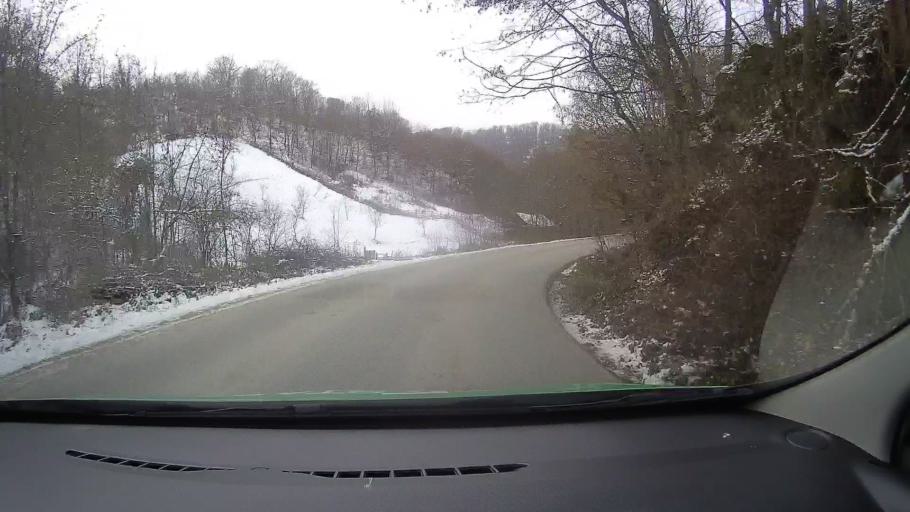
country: RO
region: Alba
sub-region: Oras Zlatna
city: Zlatna
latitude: 46.1111
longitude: 23.2049
